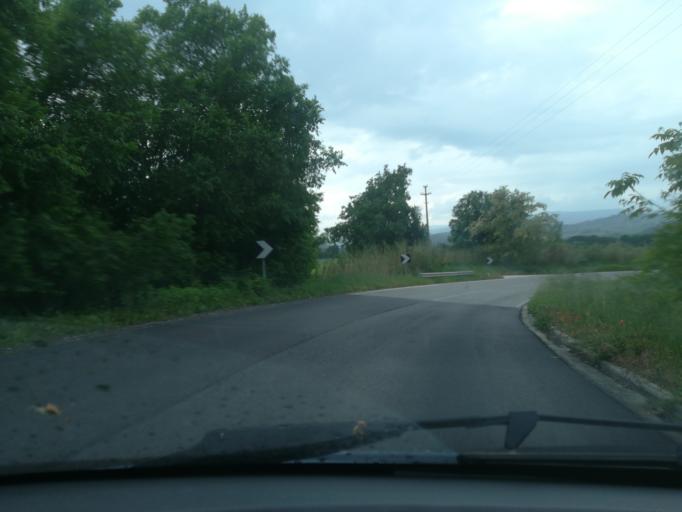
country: IT
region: The Marches
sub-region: Provincia di Macerata
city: Casette Verdini
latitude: 43.2871
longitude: 13.3829
